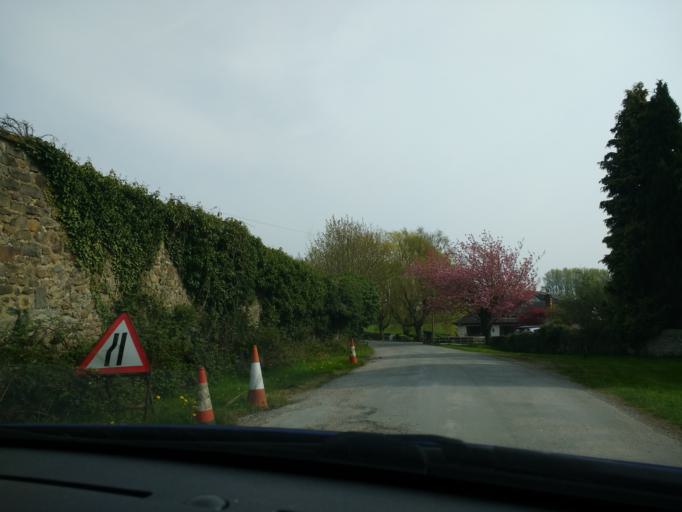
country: GB
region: England
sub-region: Lancashire
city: Lancaster
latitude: 54.0074
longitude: -2.8234
